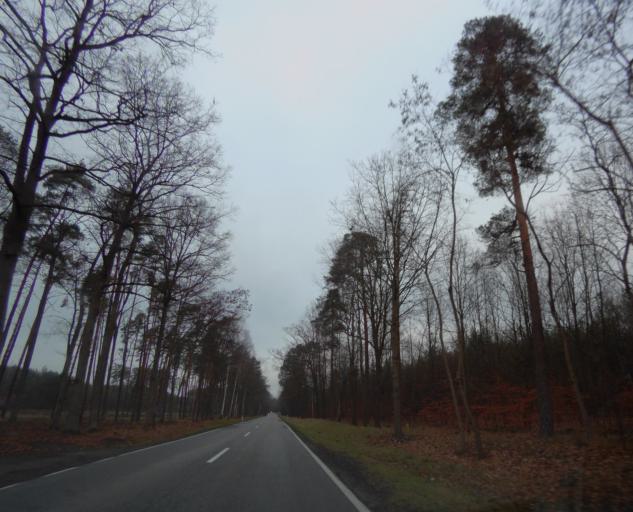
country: PL
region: Subcarpathian Voivodeship
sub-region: Powiat nizanski
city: Krzeszow
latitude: 50.3809
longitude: 22.3098
